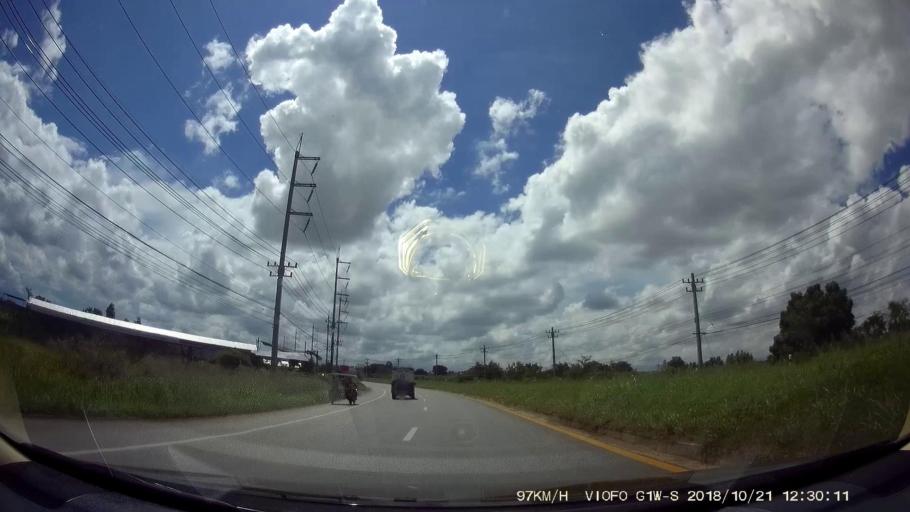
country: TH
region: Nakhon Ratchasima
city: Dan Khun Thot
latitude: 15.1747
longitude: 101.7405
